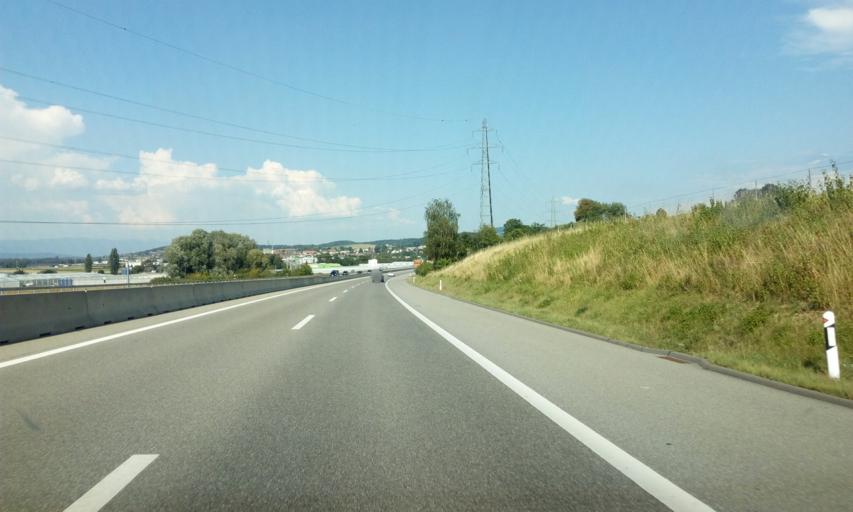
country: CH
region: Fribourg
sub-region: See District
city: Kerzers
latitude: 46.9597
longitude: 7.1743
